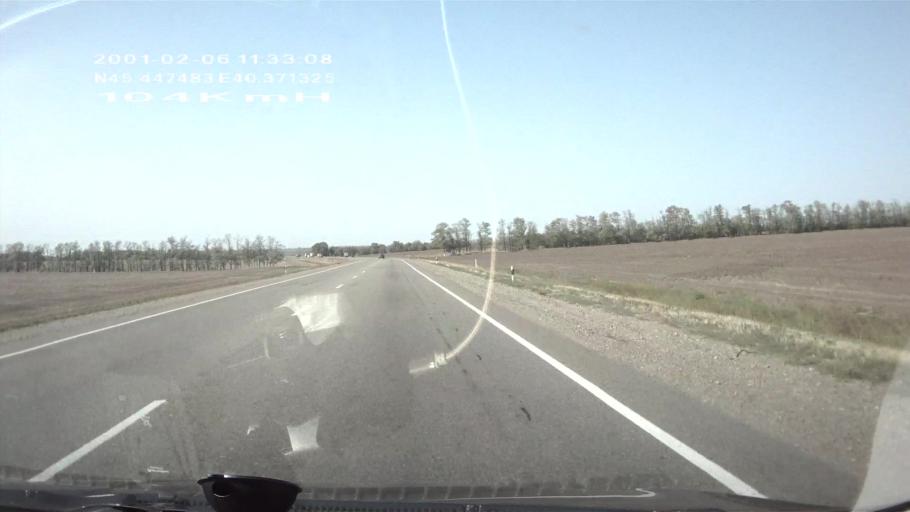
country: RU
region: Krasnodarskiy
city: Kazanskaya
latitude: 45.4471
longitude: 40.3704
